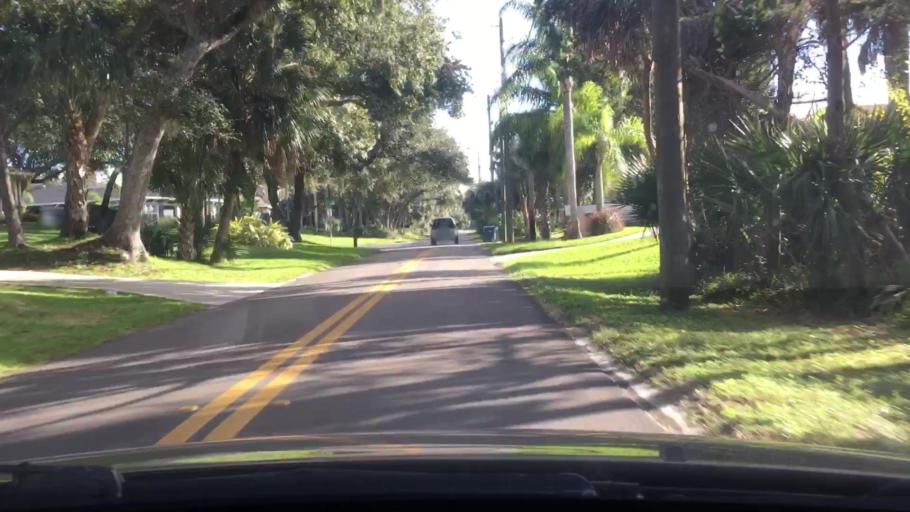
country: US
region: Florida
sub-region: Volusia County
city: Ormond-by-the-Sea
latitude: 29.3860
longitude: -81.0885
